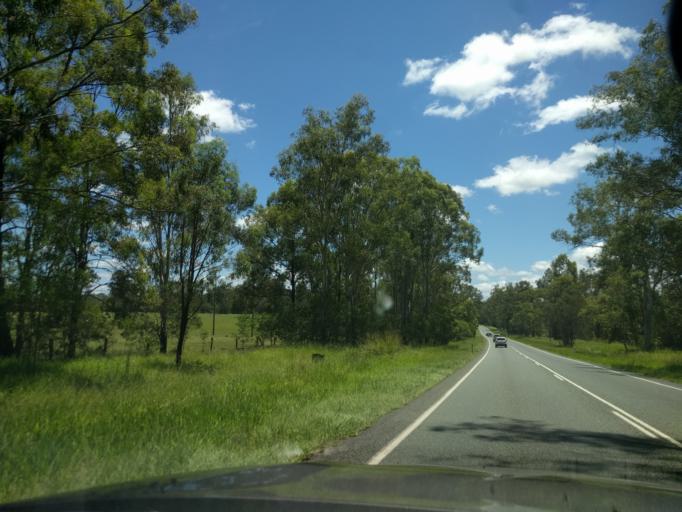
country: AU
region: Queensland
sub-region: Logan
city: Cedar Vale
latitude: -27.8516
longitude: 153.0144
